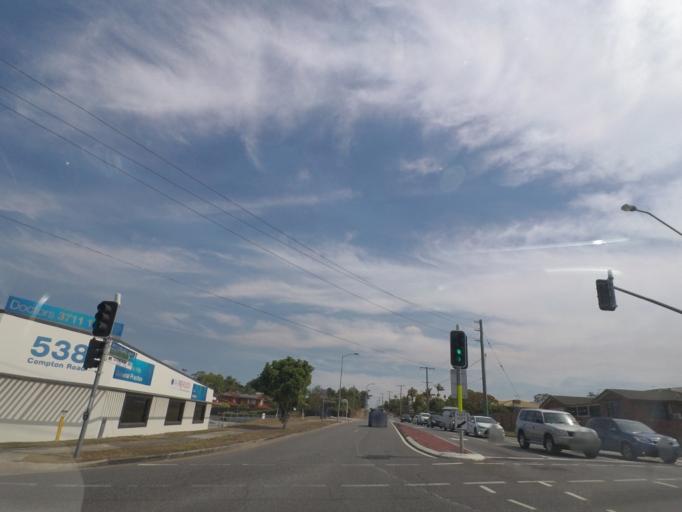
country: AU
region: Queensland
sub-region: Brisbane
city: Sunnybank Hills
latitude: -27.6114
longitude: 153.0621
